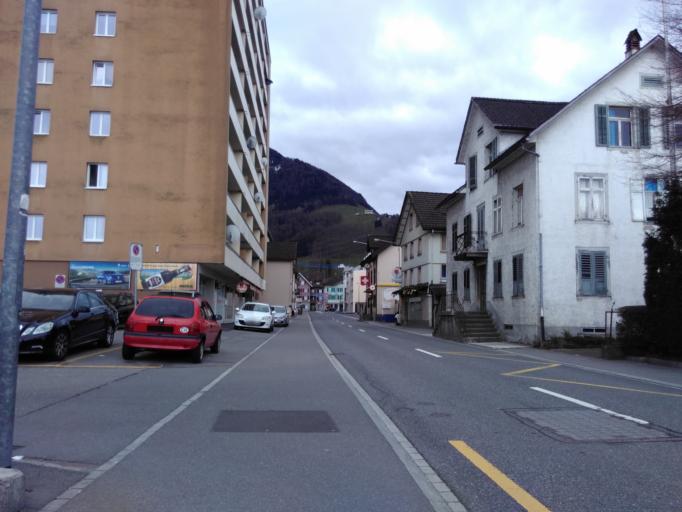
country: CH
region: Schwyz
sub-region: Bezirk March
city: Schubelbach
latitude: 47.1764
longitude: 8.8978
